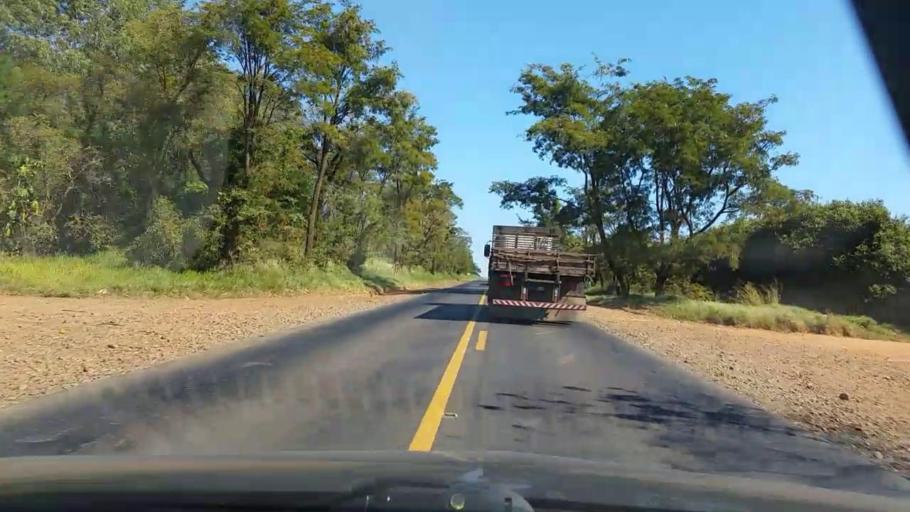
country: BR
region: Sao Paulo
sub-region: Sao Manuel
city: Sao Manuel
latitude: -22.8130
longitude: -48.6789
